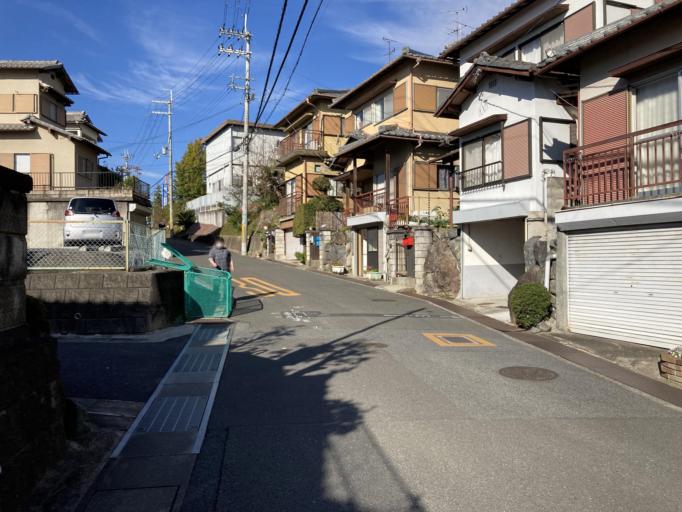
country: JP
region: Nara
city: Nara-shi
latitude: 34.6697
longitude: 135.7723
